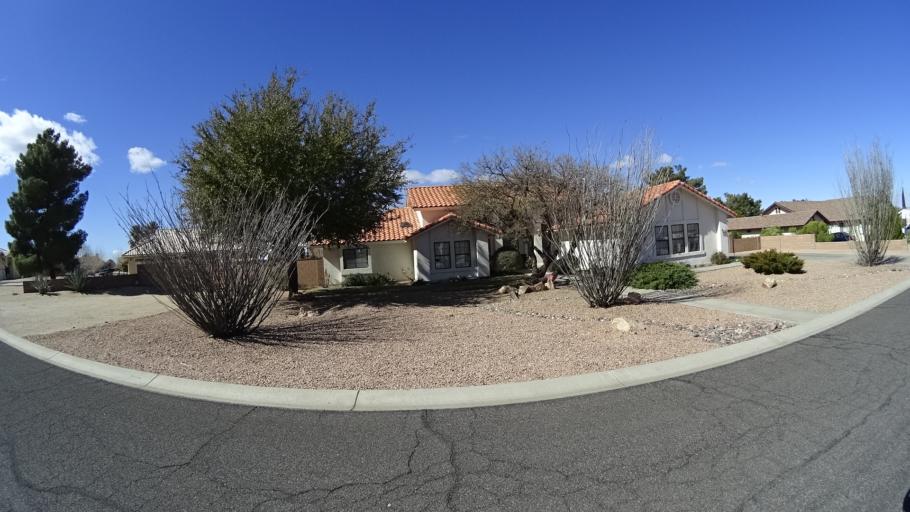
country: US
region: Arizona
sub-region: Mohave County
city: Kingman
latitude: 35.2000
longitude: -113.9734
